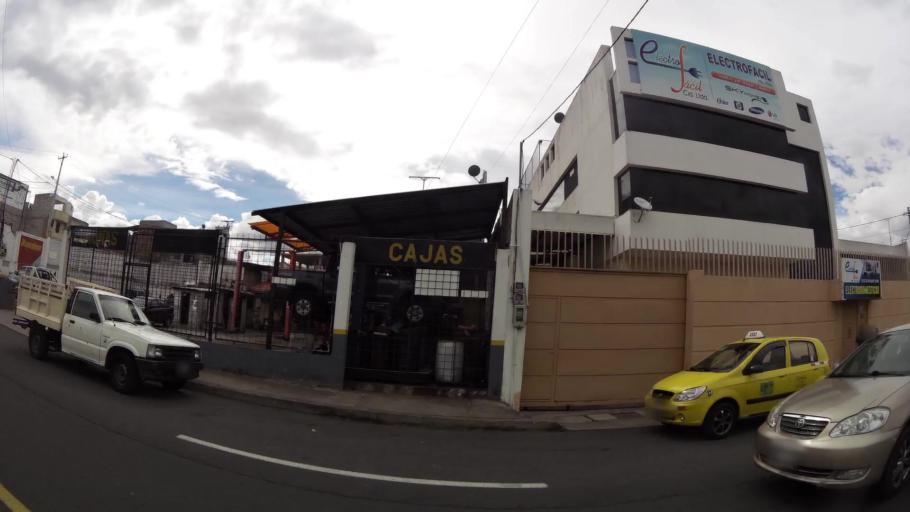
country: EC
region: Tungurahua
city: Ambato
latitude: -1.2766
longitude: -78.6275
